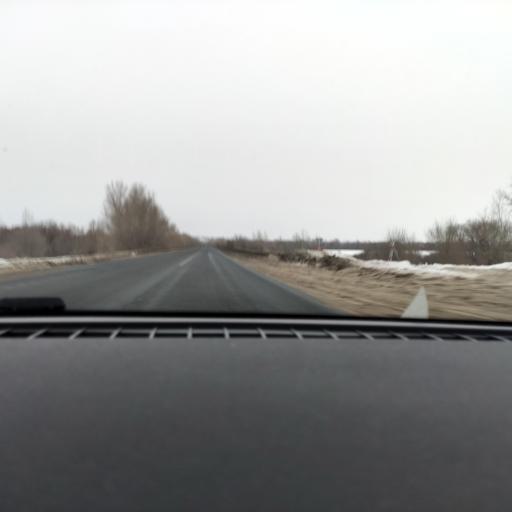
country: RU
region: Samara
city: Smyshlyayevka
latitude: 53.2073
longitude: 50.5073
